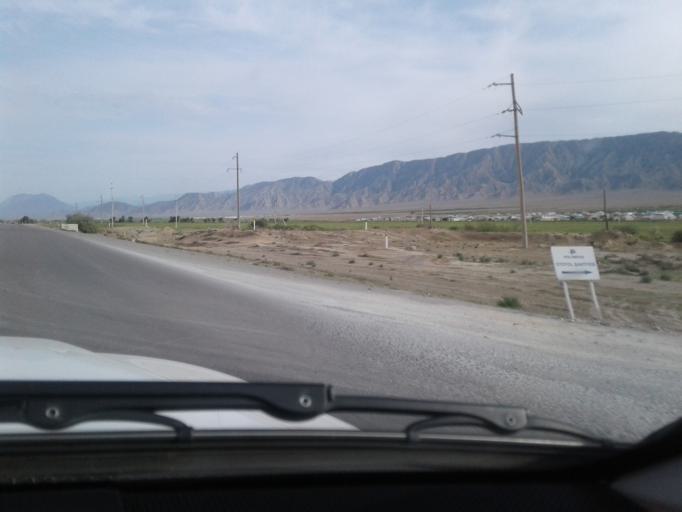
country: TM
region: Ahal
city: Arcabil
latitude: 38.2105
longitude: 57.8130
